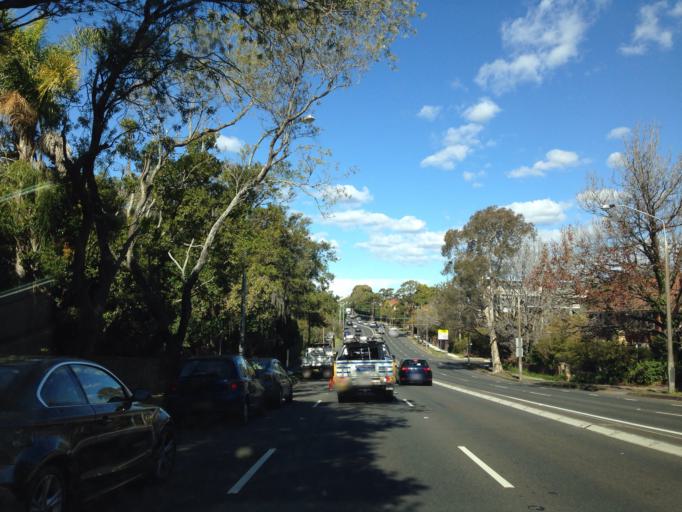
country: AU
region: New South Wales
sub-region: Ku-ring-gai
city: Killara
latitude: -33.7576
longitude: 151.1534
